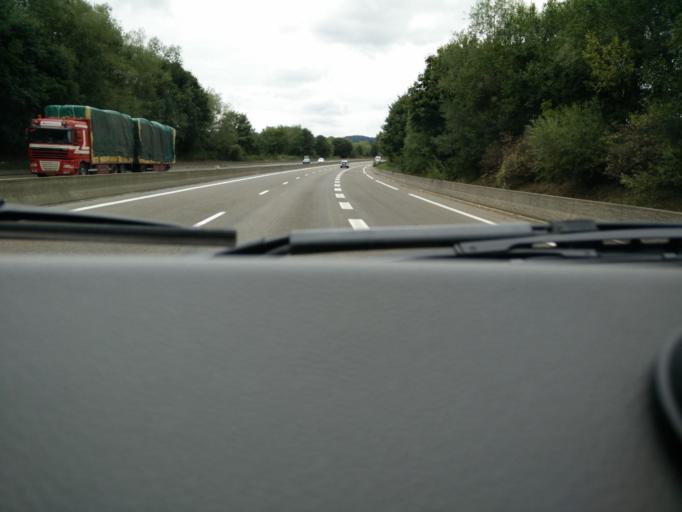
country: FR
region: Champagne-Ardenne
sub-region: Departement des Ardennes
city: Balan
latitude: 49.6823
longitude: 4.9672
